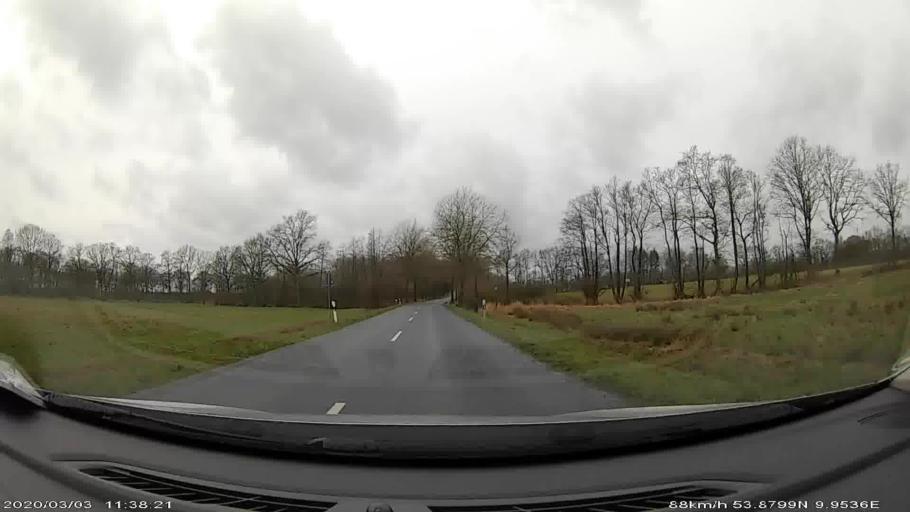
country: DE
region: Schleswig-Holstein
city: Schmalfeld
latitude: 53.8805
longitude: 9.9486
